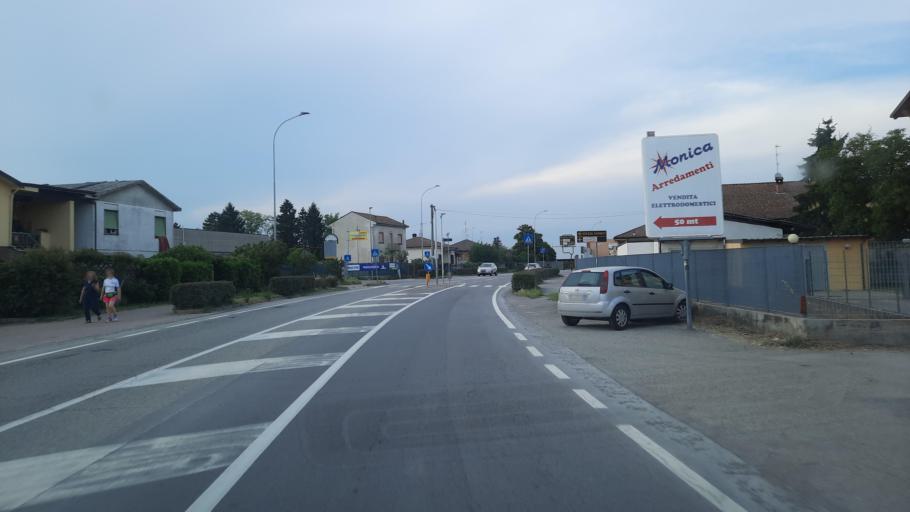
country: IT
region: Lombardy
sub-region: Provincia di Pavia
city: Garlasco
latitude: 45.1939
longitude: 8.9137
